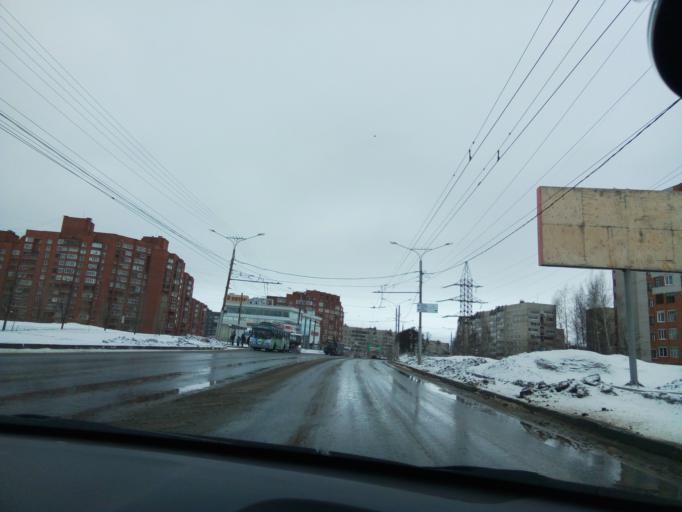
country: RU
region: Chuvashia
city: Novyye Lapsary
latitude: 56.1352
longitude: 47.1641
